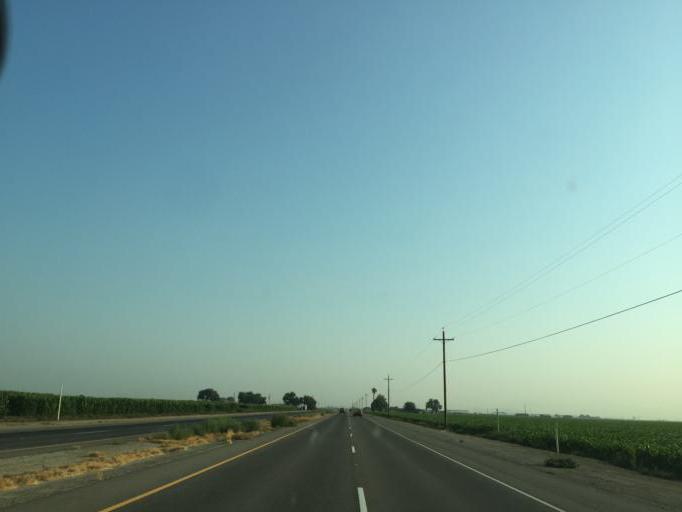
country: US
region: California
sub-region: Tulare County
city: London
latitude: 36.4469
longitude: -119.3947
